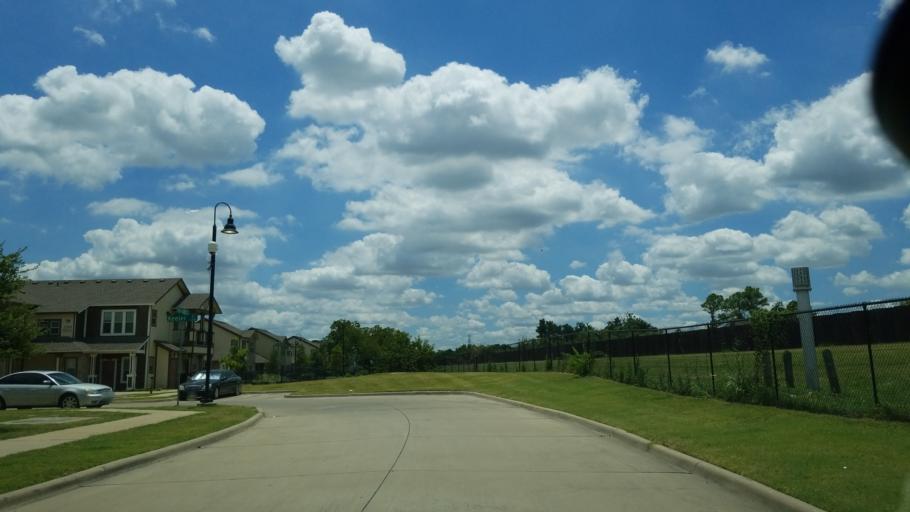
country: US
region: Texas
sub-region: Dallas County
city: Dallas
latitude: 32.7380
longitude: -96.7563
